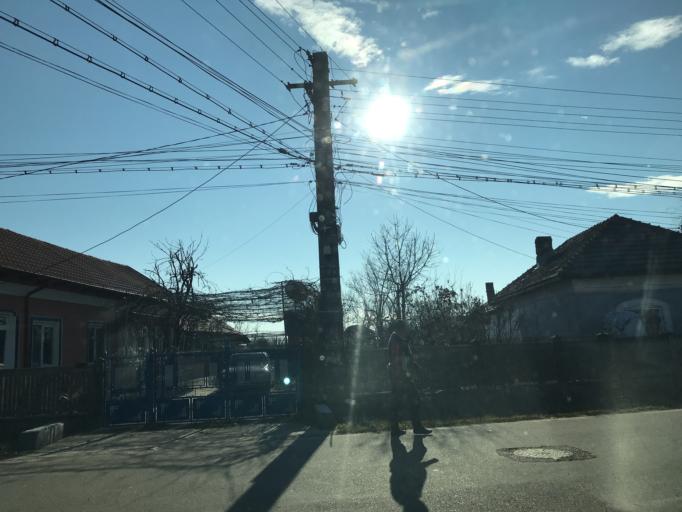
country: RO
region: Olt
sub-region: Comuna Slatioara
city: Slatioara
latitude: 44.3990
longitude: 24.3201
